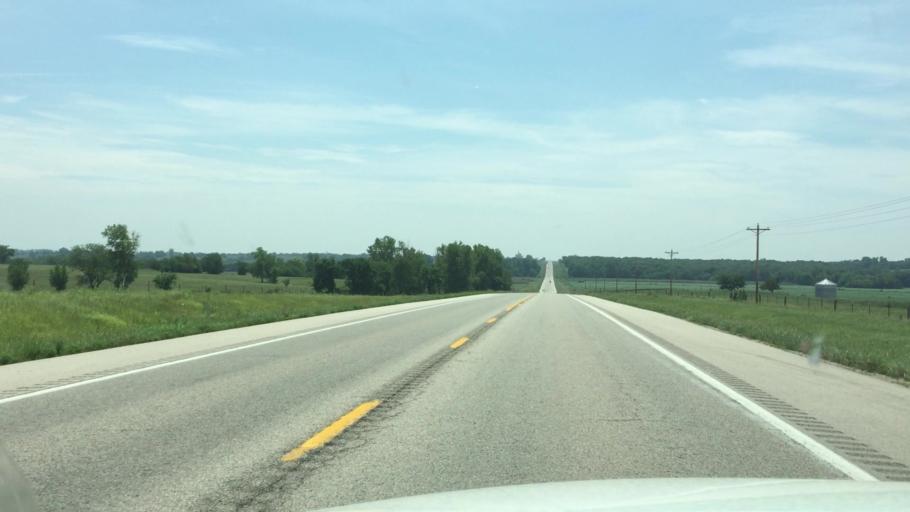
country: US
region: Kansas
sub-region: Jackson County
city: Holton
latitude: 39.6431
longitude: -95.7310
